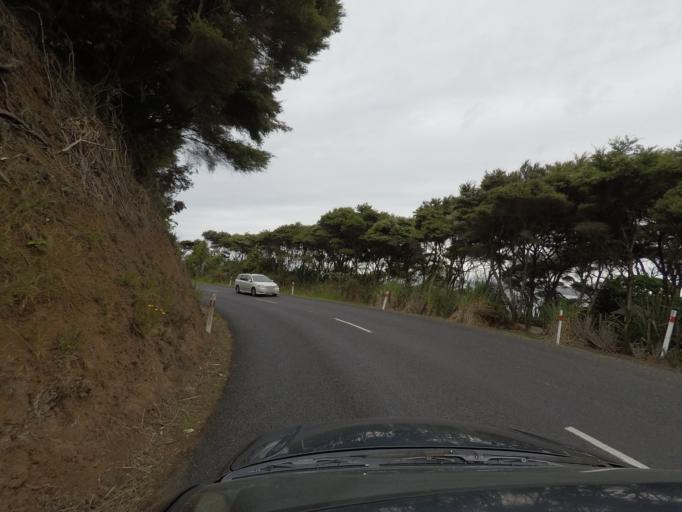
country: NZ
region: Waikato
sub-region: Waikato District
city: Raglan
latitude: -37.8237
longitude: 174.8150
